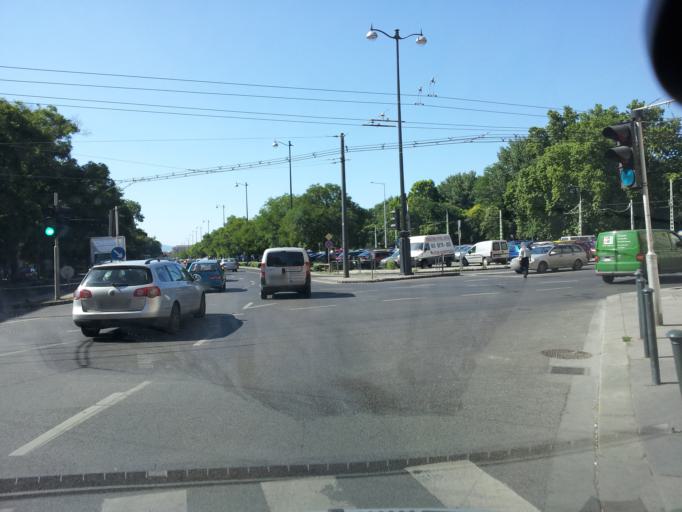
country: HU
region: Budapest
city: Budapest VII. keruelet
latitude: 47.5066
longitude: 19.0860
